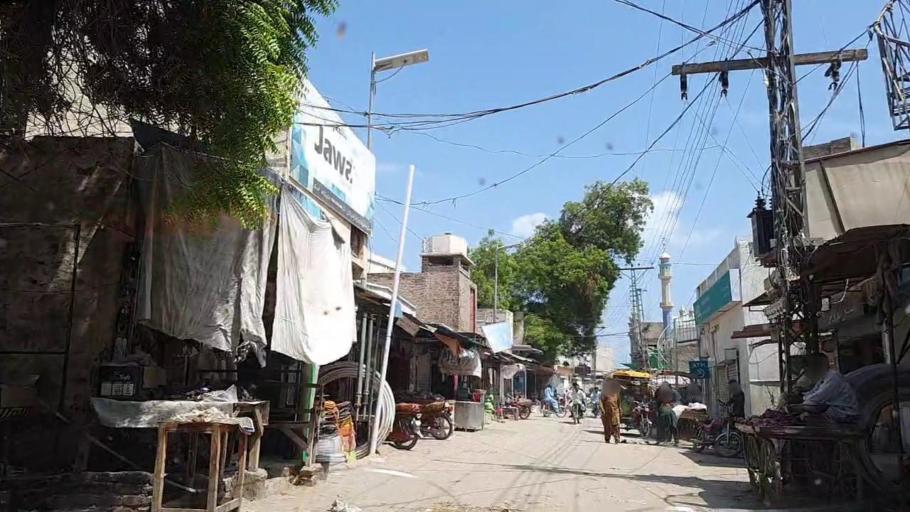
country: PK
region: Sindh
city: Tharu Shah
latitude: 26.9429
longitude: 68.1170
